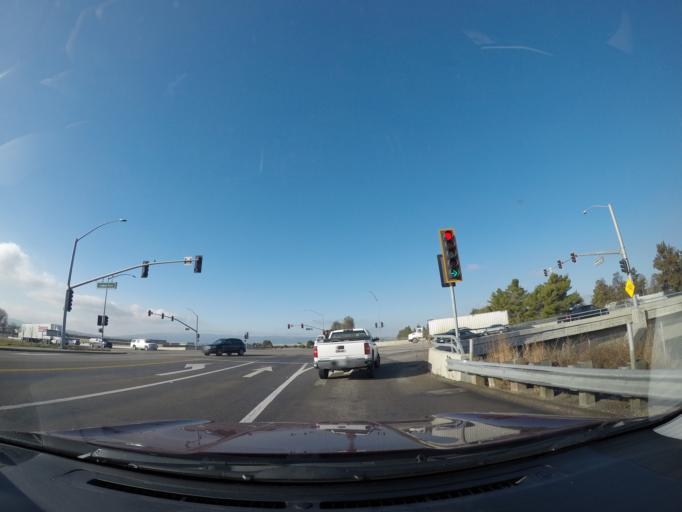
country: US
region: California
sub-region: Alameda County
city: Livermore
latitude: 37.6965
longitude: -121.8047
